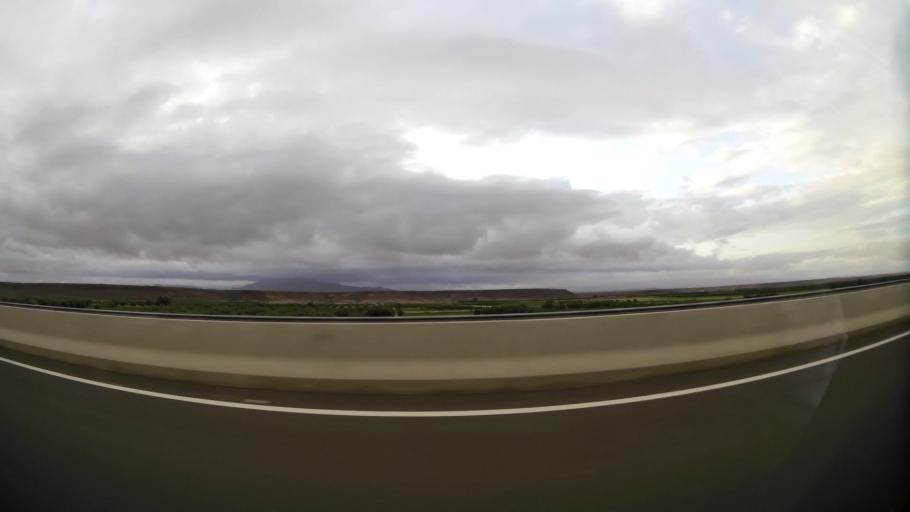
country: MA
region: Taza-Al Hoceima-Taounate
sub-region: Taza
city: Guercif
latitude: 34.3982
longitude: -3.2018
